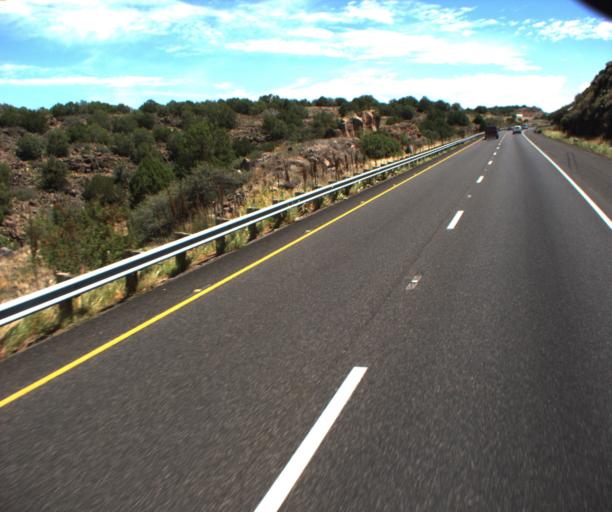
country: US
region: Arizona
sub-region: Yavapai County
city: Big Park
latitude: 34.7182
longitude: -111.7218
